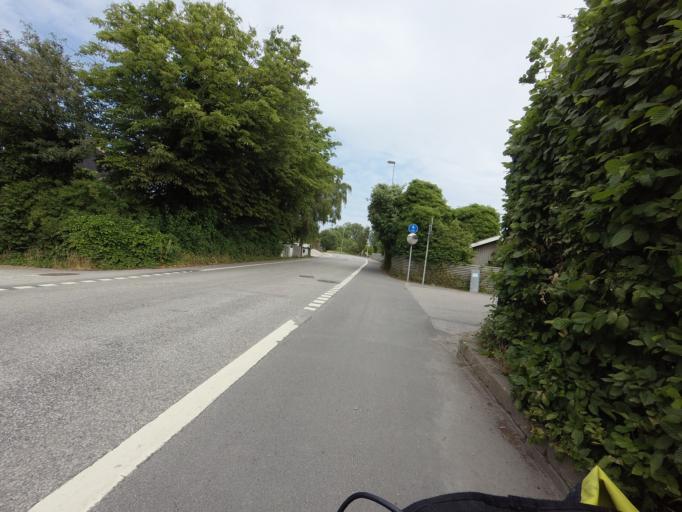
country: SE
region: Skane
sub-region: Malmo
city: Bunkeflostrand
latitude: 55.5361
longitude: 12.9215
